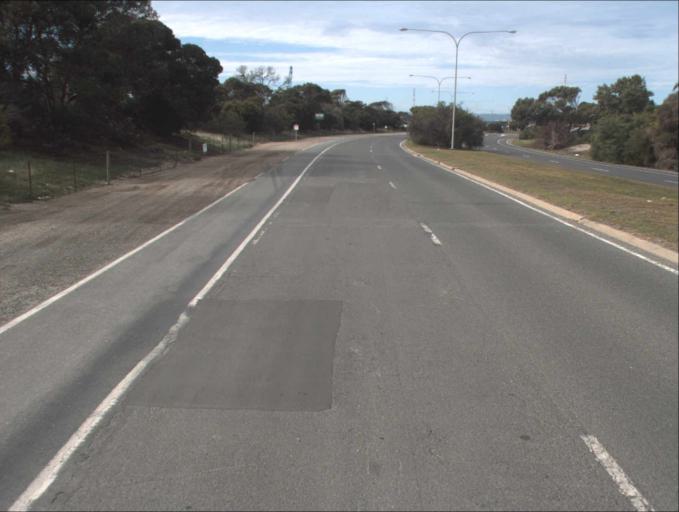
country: AU
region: South Australia
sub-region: Port Adelaide Enfield
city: Birkenhead
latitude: -34.7809
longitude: 138.4977
